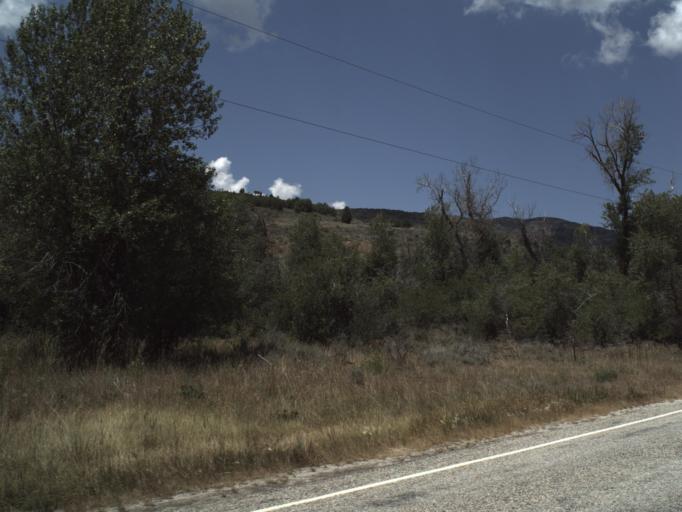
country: US
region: Utah
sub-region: Weber County
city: Wolf Creek
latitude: 41.3057
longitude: -111.6170
